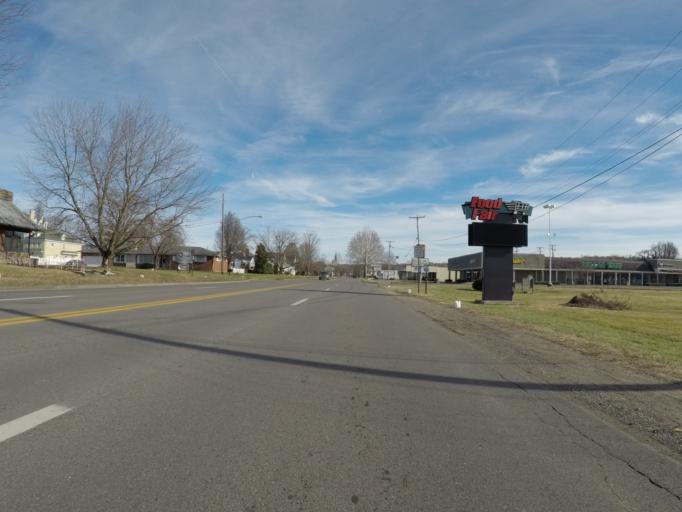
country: US
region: West Virginia
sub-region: Wayne County
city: Ceredo
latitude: 38.3970
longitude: -82.5633
